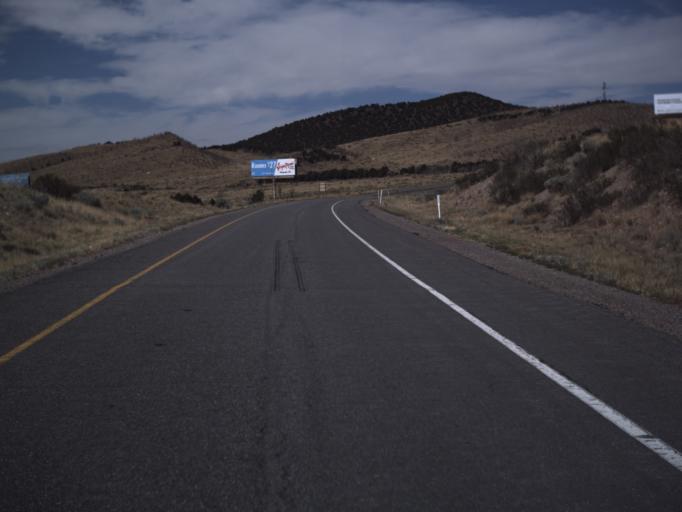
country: US
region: Utah
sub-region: Beaver County
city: Beaver
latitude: 38.6171
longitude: -112.6078
